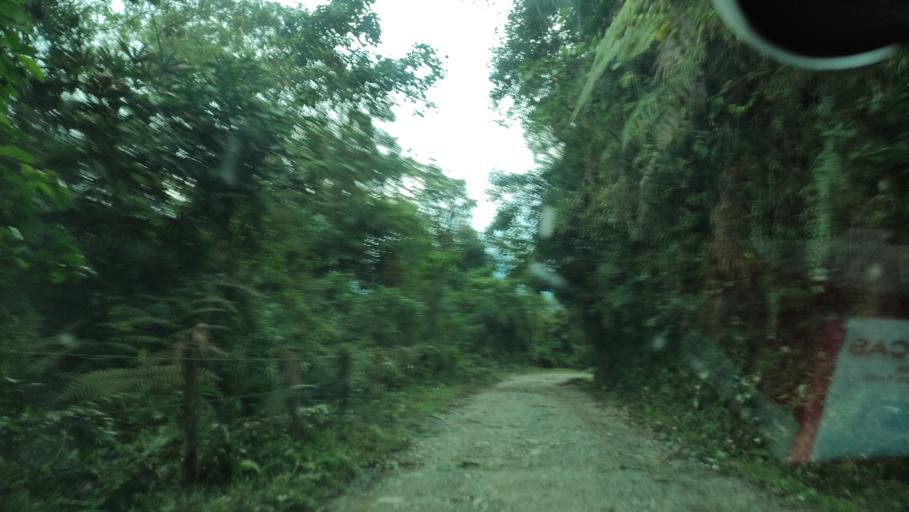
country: CO
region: Valle del Cauca
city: San Pedro
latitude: 3.8801
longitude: -76.1523
